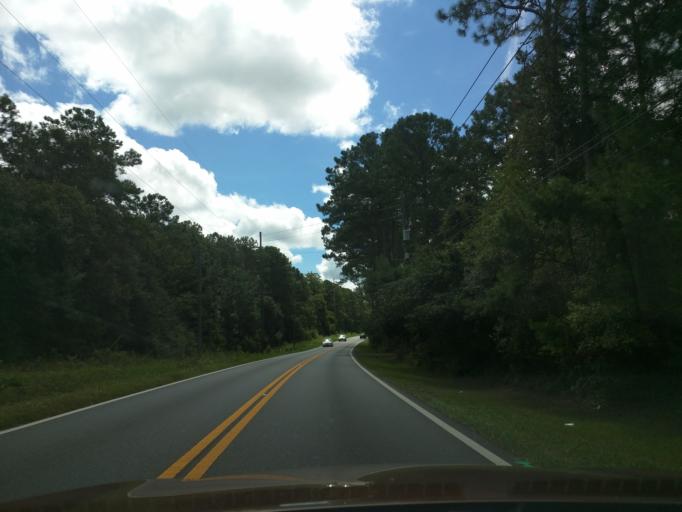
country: US
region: Florida
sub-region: Leon County
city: Tallahassee
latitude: 30.5776
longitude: -84.2346
